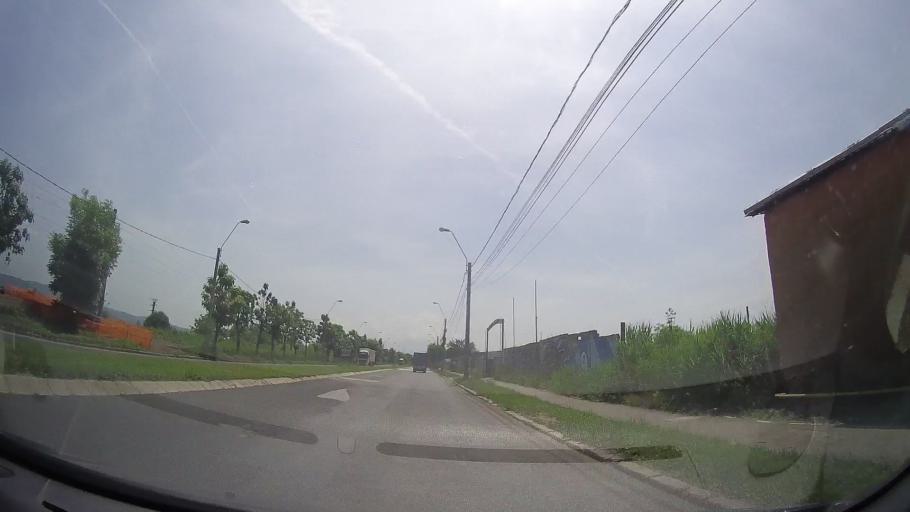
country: RO
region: Hunedoara
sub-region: Municipiul Deva
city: Deva
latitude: 45.8948
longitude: 22.8993
